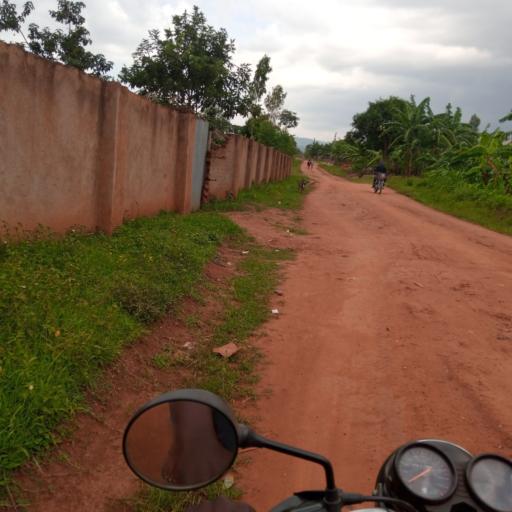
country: UG
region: Eastern Region
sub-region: Mbale District
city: Mbale
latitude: 1.1201
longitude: 34.1787
